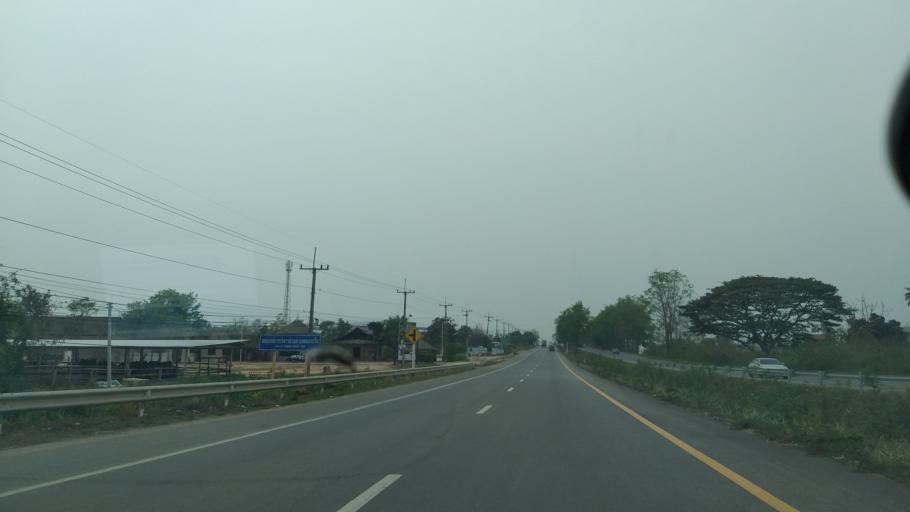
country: TH
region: Chachoengsao
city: Plaeng Yao
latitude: 13.5003
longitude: 101.2714
